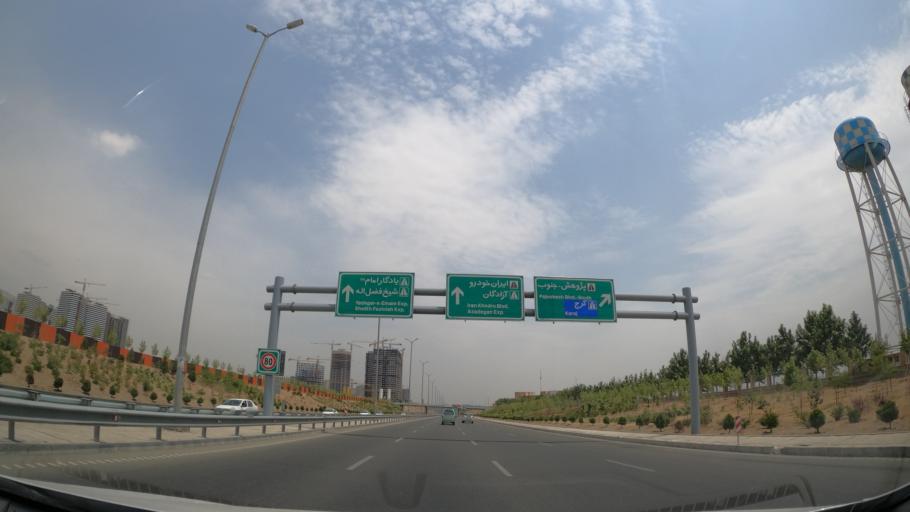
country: IR
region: Tehran
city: Shahr-e Qods
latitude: 35.7509
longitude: 51.1705
